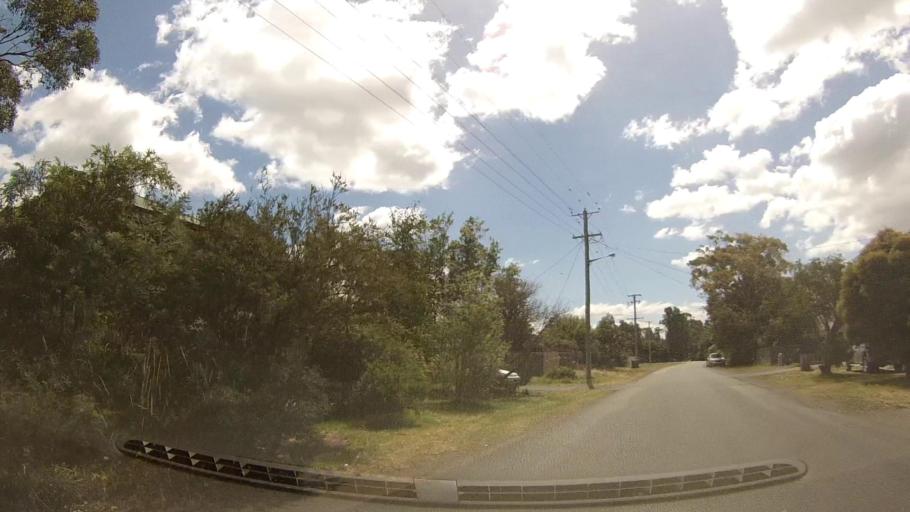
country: AU
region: Tasmania
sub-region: Clarence
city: Seven Mile Beach
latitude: -42.8571
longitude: 147.5095
